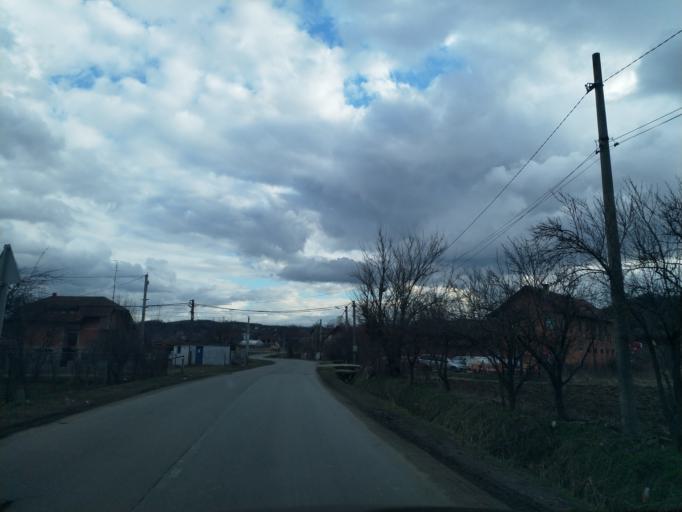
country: RS
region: Central Serbia
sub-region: Belgrade
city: Grocka
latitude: 44.5771
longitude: 20.7417
